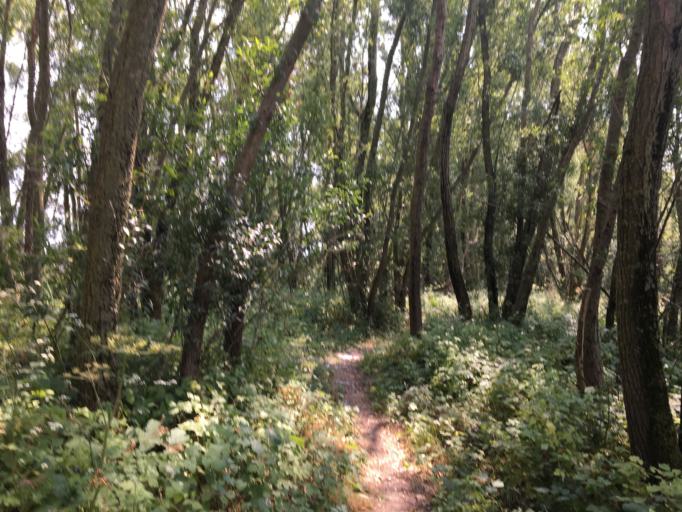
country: NL
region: Gelderland
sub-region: Gemeente Buren
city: Lienden
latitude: 51.9563
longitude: 5.5399
